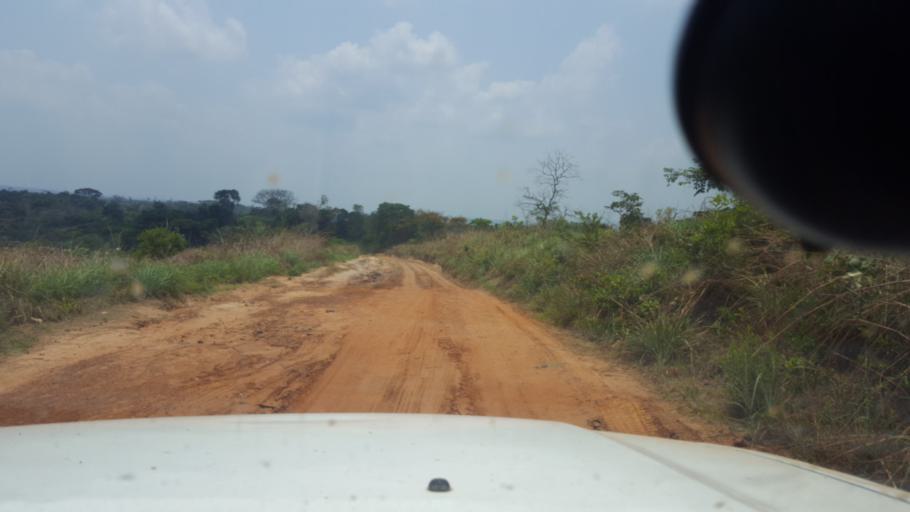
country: CD
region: Bandundu
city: Mushie
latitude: -3.7562
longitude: 16.6253
